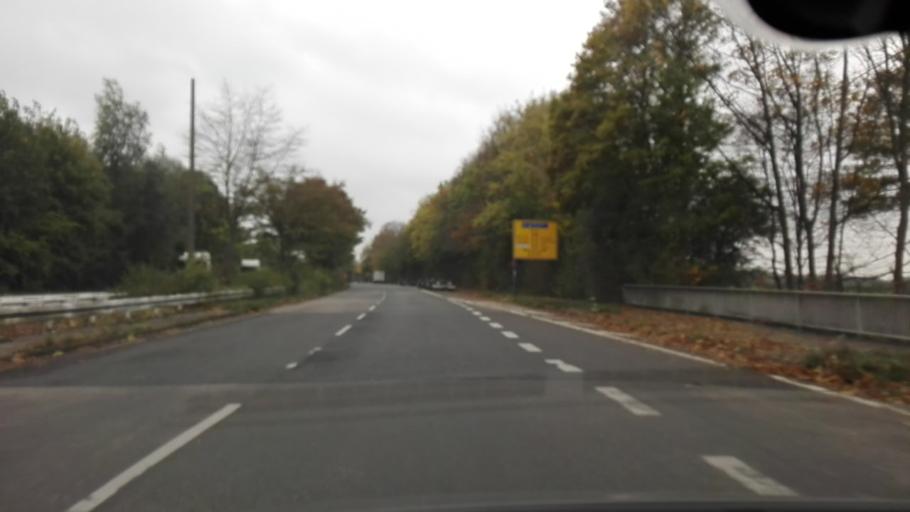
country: DE
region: North Rhine-Westphalia
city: Witten
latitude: 51.4848
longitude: 7.4014
